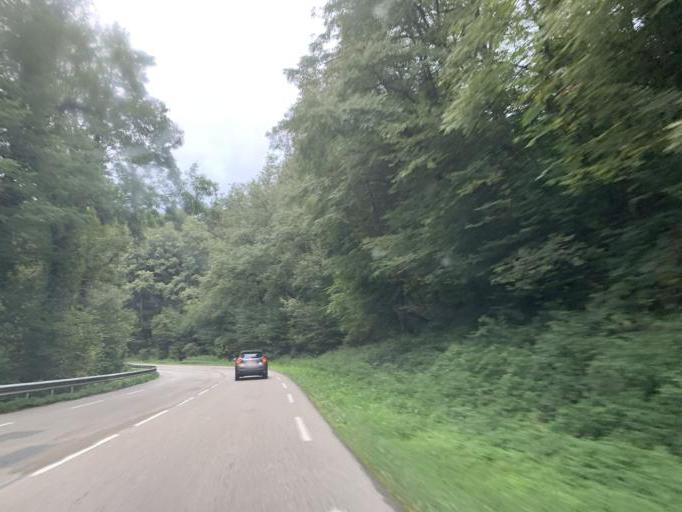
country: FR
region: Rhone-Alpes
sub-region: Departement de l'Ain
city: Belley
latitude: 45.7317
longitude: 5.6677
